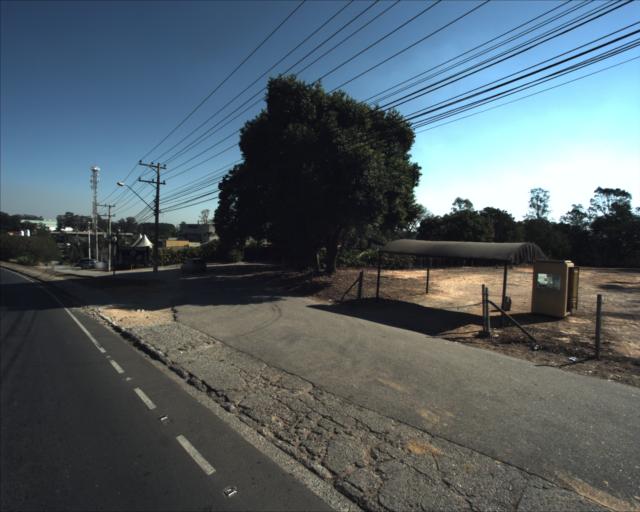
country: BR
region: Sao Paulo
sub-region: Sorocaba
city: Sorocaba
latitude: -23.4609
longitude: -47.4222
